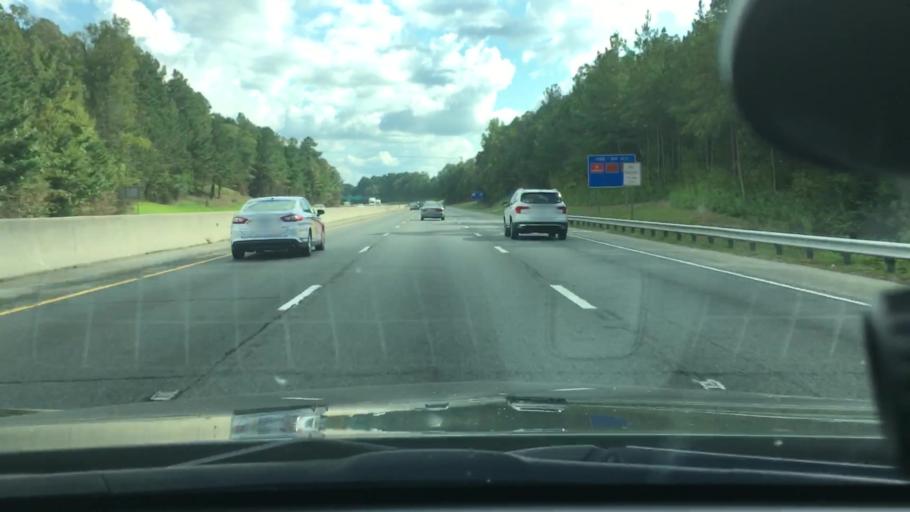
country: US
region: North Carolina
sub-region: Orange County
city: Chapel Hill
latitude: 35.9228
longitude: -78.9859
